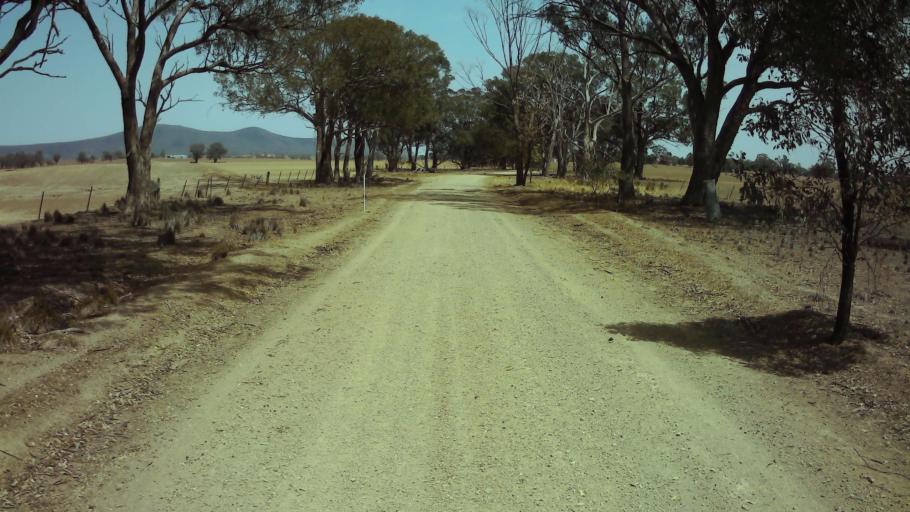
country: AU
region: New South Wales
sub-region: Weddin
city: Grenfell
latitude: -33.8841
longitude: 148.0769
